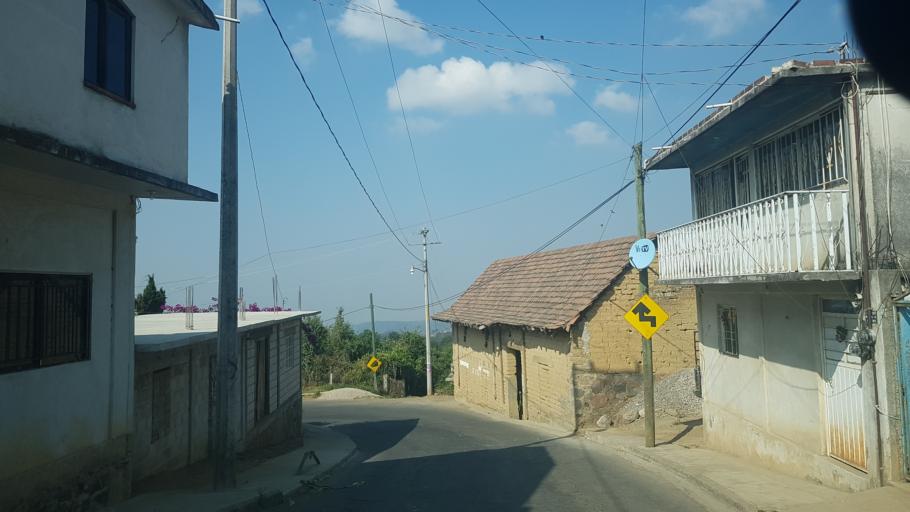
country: MX
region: Puebla
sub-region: Tochimilco
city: Santa Cruz Cuautomatitla
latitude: 18.8947
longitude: -98.6741
